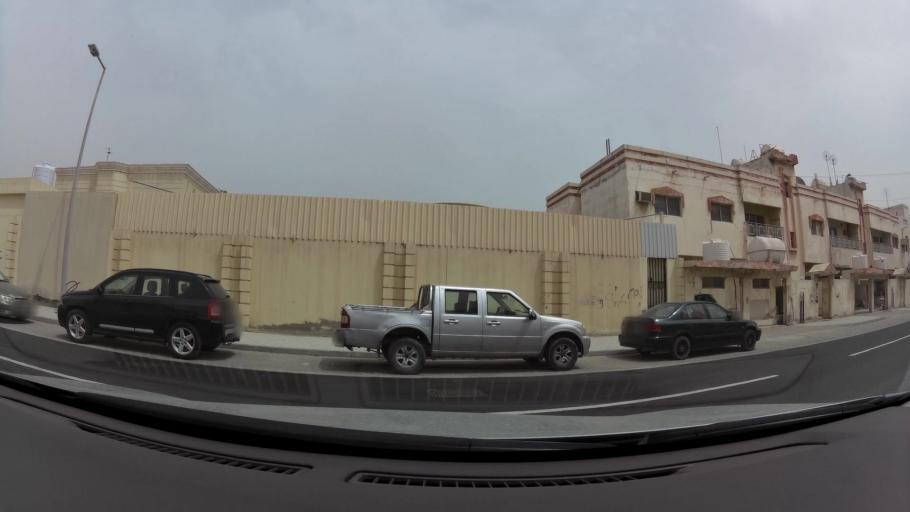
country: QA
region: Baladiyat ad Dawhah
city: Doha
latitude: 25.2460
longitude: 51.5596
